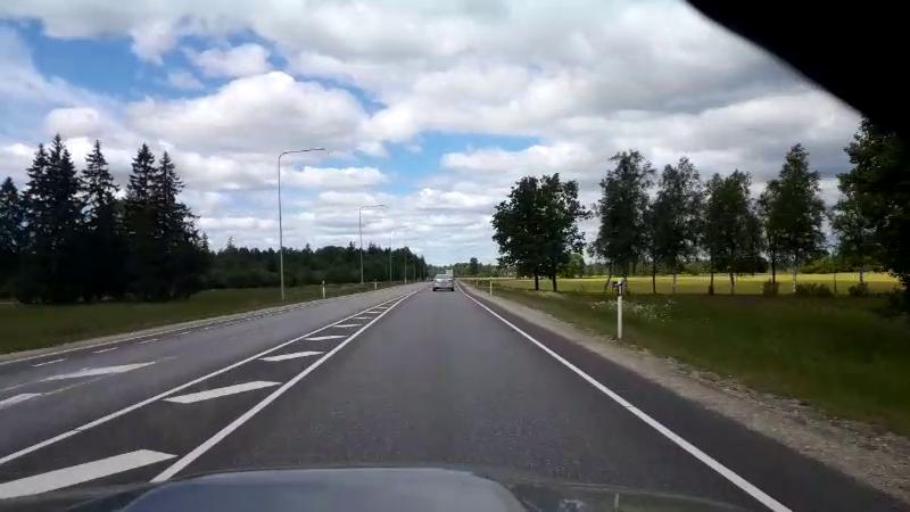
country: EE
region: Paernumaa
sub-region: Halinga vald
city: Parnu-Jaagupi
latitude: 58.6230
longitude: 24.5090
